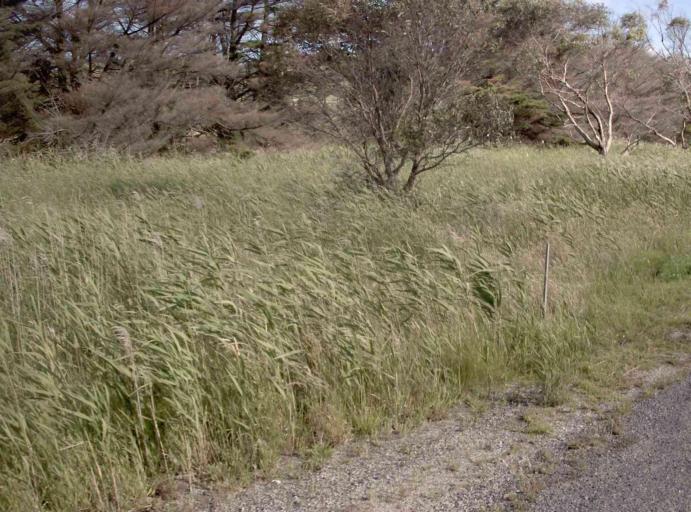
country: AU
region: Victoria
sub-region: Bass Coast
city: North Wonthaggi
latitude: -38.5106
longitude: 145.4499
